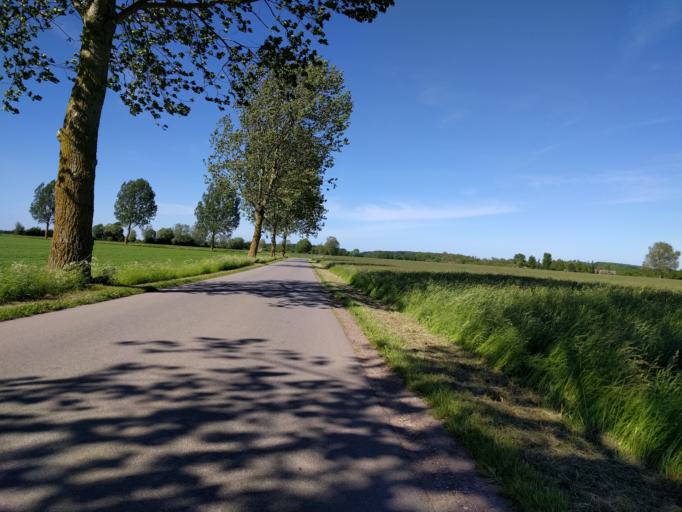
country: DK
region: South Denmark
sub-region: Kerteminde Kommune
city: Kerteminde
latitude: 55.4209
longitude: 10.6602
